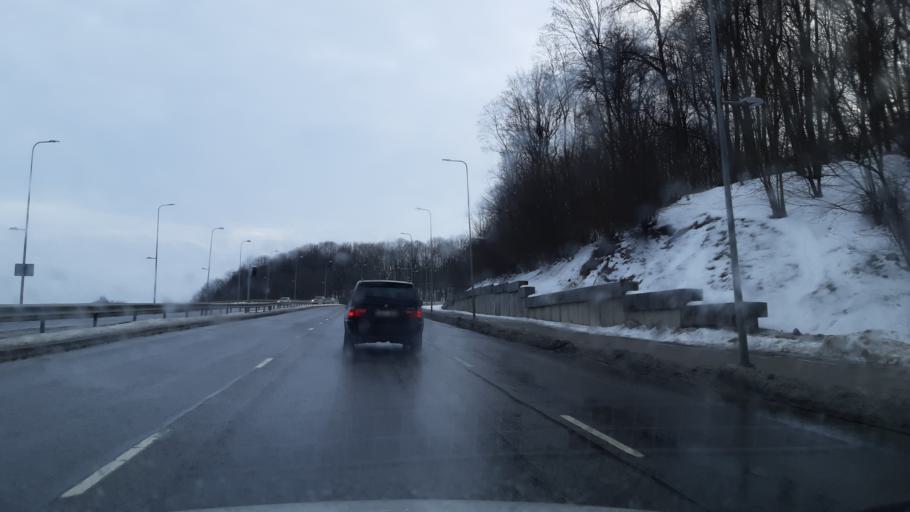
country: LT
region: Kauno apskritis
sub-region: Kaunas
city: Aleksotas
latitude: 54.8766
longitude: 23.9216
